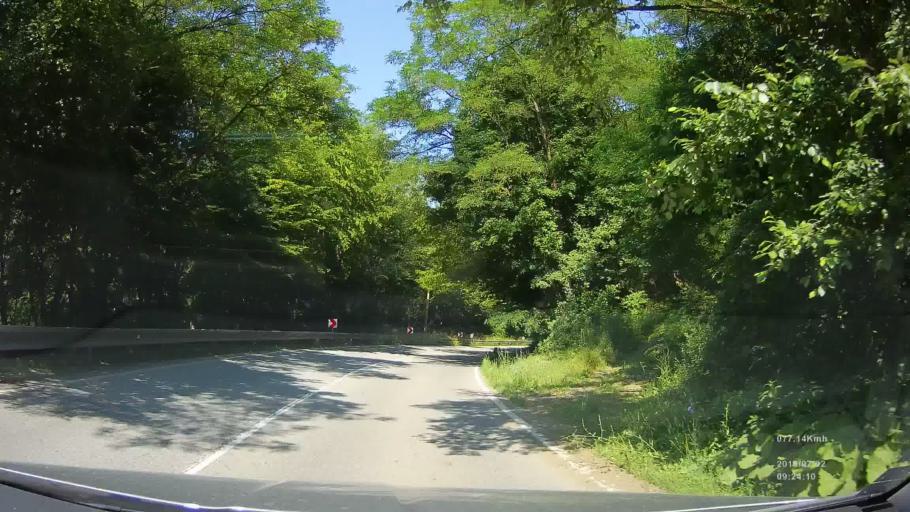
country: SK
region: Kosicky
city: Kosice
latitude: 48.7521
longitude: 21.2014
